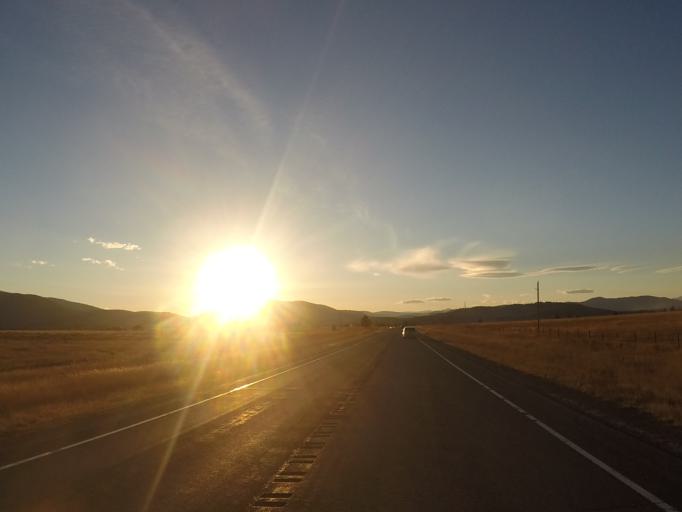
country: US
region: Montana
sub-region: Missoula County
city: Seeley Lake
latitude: 47.0201
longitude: -113.1086
